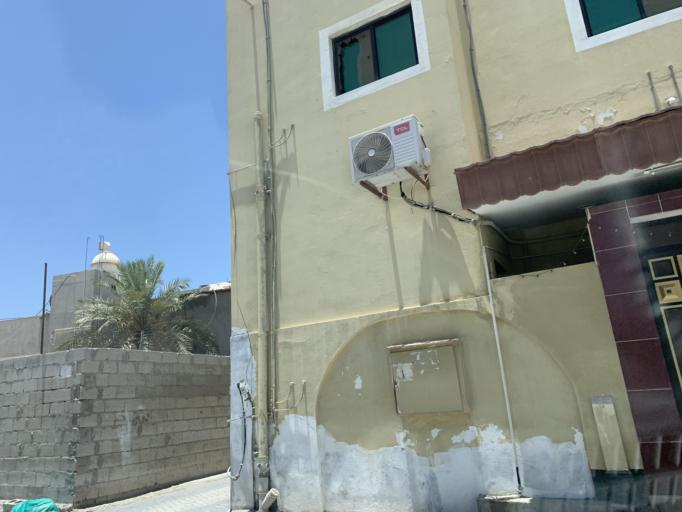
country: BH
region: Manama
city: Jidd Hafs
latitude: 26.2290
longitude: 50.4820
